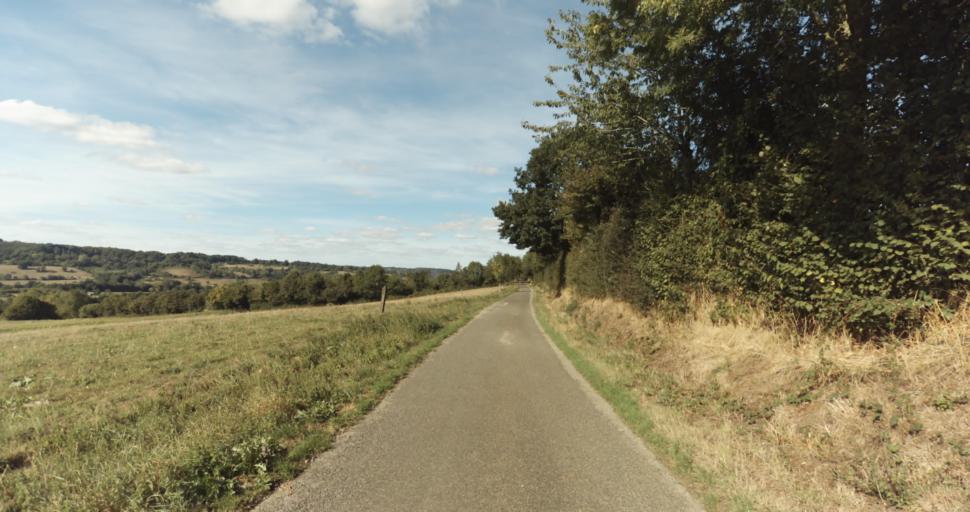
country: FR
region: Lower Normandy
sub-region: Departement de l'Orne
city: Vimoutiers
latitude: 48.9312
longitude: 0.1198
